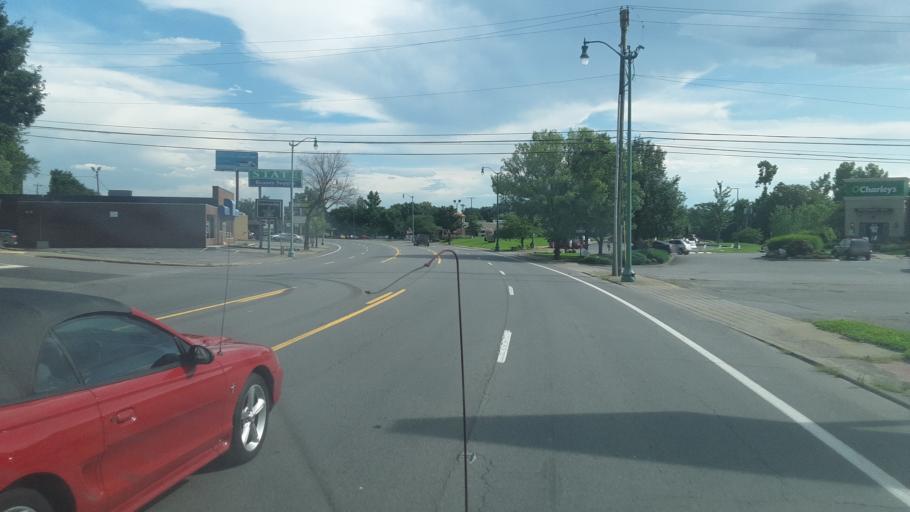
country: US
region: Tennessee
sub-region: Montgomery County
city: Clarksville
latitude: 36.5380
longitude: -87.3673
